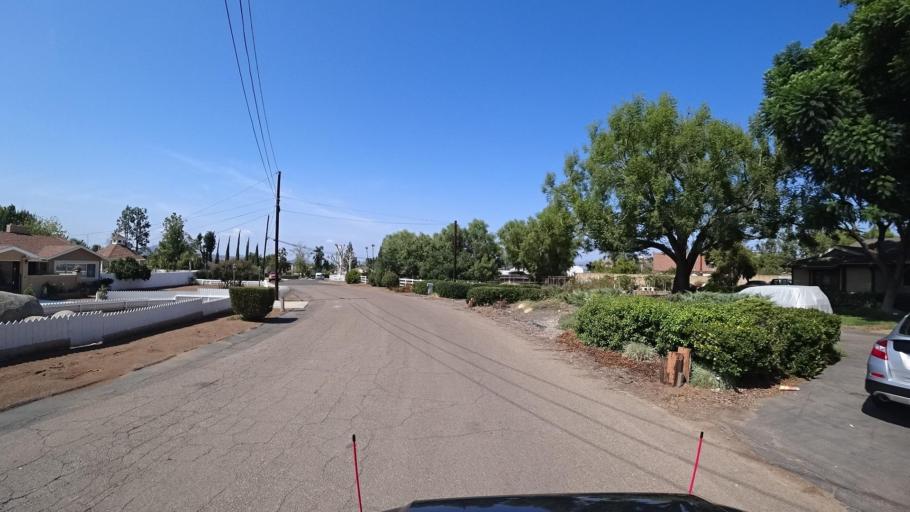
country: US
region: California
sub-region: San Diego County
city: Granite Hills
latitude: 32.7844
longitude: -116.9172
